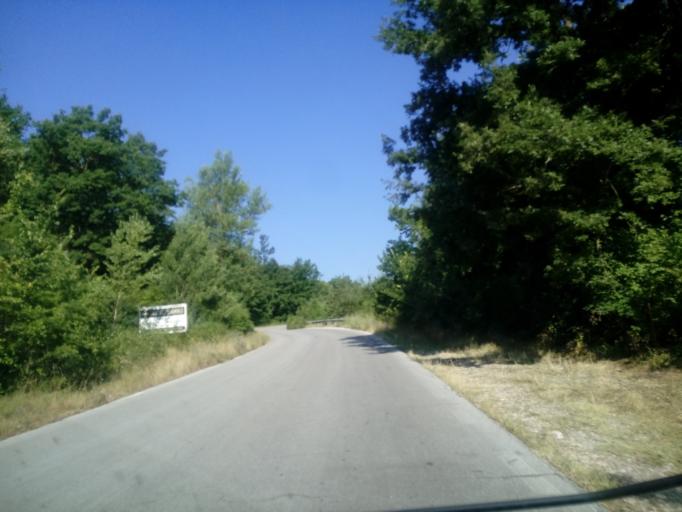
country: IT
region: Molise
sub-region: Provincia di Campobasso
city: Jelsi
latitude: 41.5105
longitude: 14.7835
